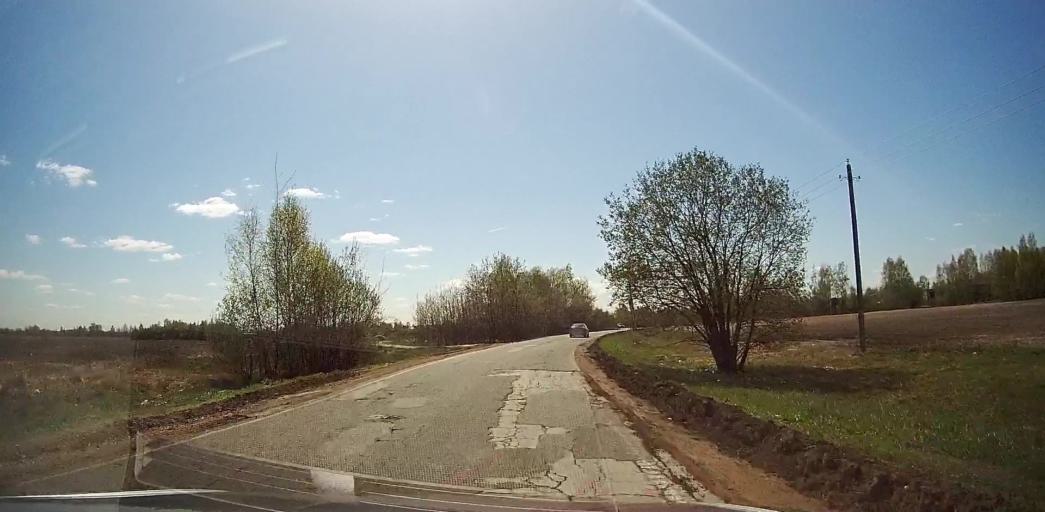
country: RU
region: Moskovskaya
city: Malyshevo
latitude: 55.4627
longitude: 38.3818
